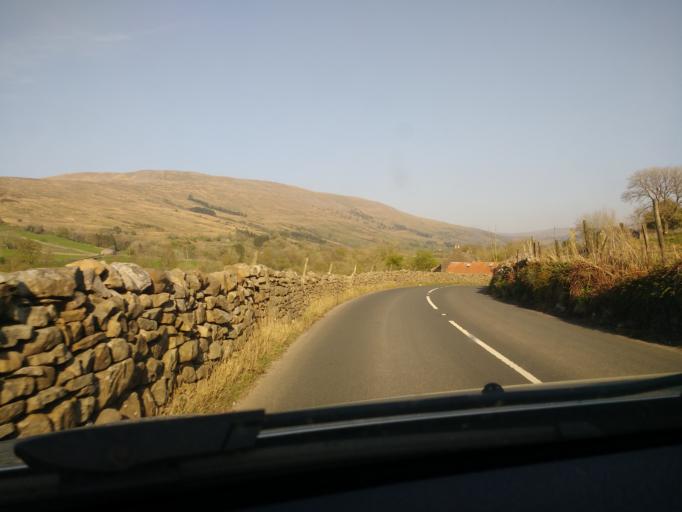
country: GB
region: England
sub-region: Cumbria
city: Sedbergh
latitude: 54.3138
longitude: -2.4622
